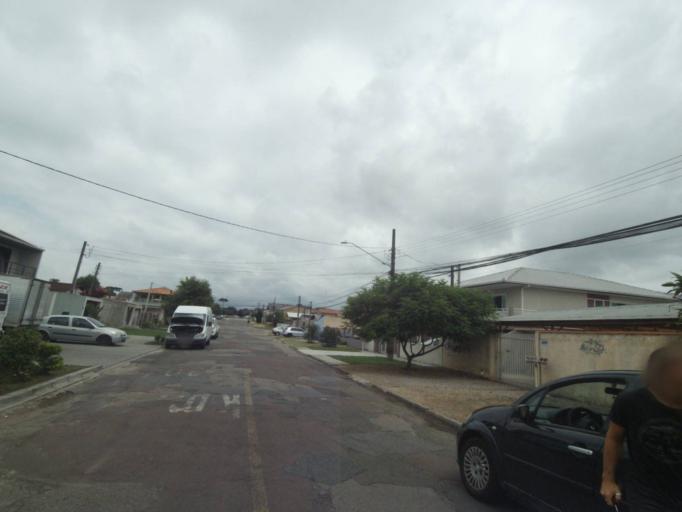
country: BR
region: Parana
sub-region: Pinhais
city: Pinhais
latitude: -25.4585
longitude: -49.2053
